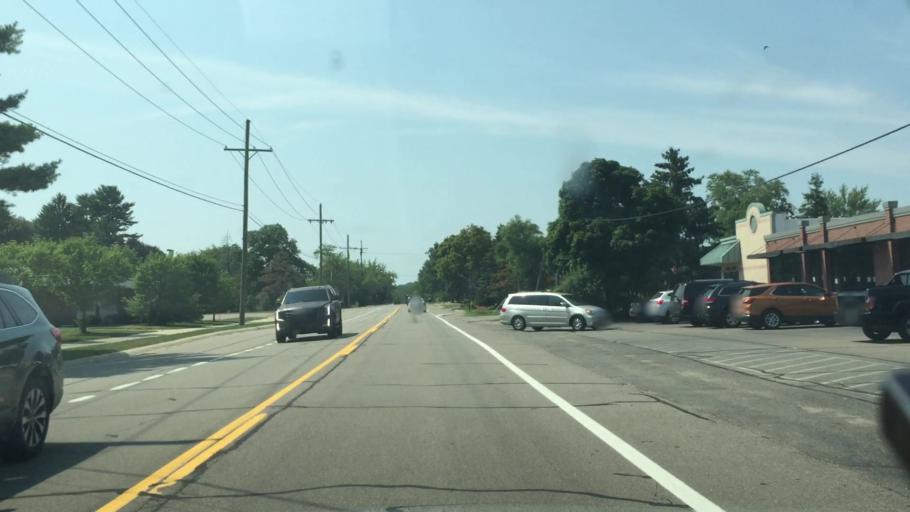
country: US
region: Michigan
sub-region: Oakland County
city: Franklin
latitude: 42.5520
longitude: -83.3239
